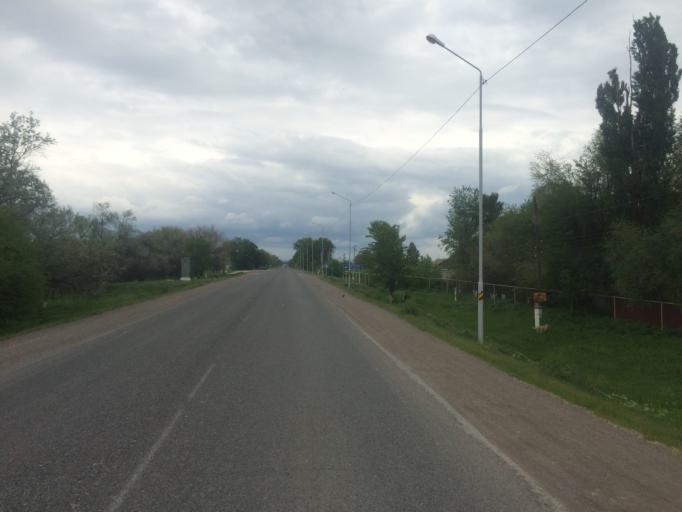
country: KZ
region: Zhambyl
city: Georgiyevka
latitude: 43.2266
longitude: 74.4016
